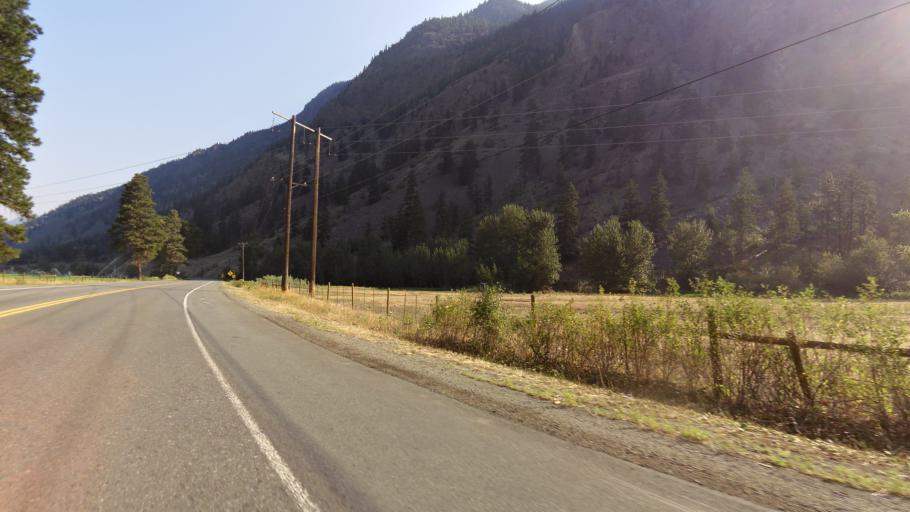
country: CA
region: British Columbia
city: Oliver
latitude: 49.2584
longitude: -120.0148
